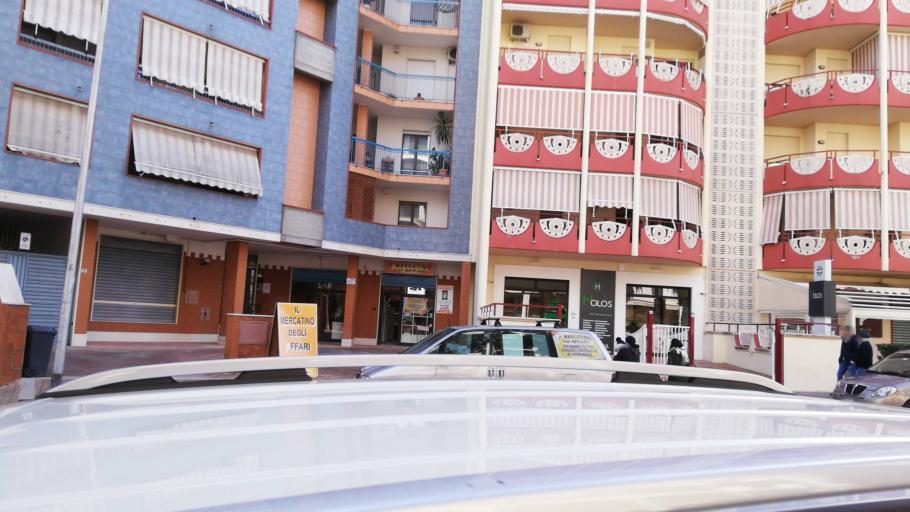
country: IT
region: Apulia
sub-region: Provincia di Barletta - Andria - Trani
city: Andria
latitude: 41.2343
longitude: 16.3015
